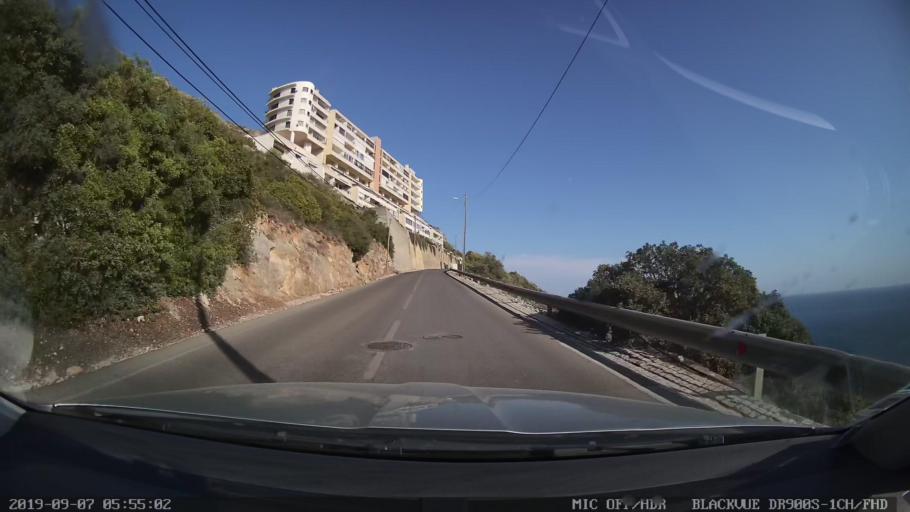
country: PT
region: Setubal
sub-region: Sesimbra
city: Sesimbra
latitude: 38.4433
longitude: -9.0930
